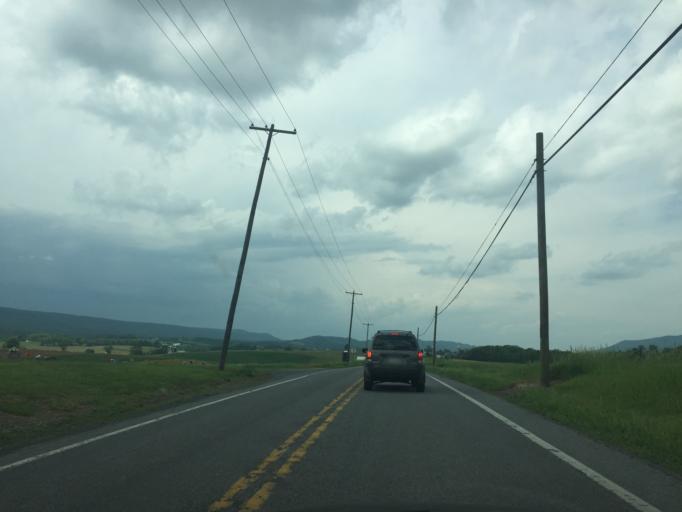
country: US
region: Pennsylvania
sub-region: Fulton County
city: McConnellsburg
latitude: 39.8809
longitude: -78.0186
